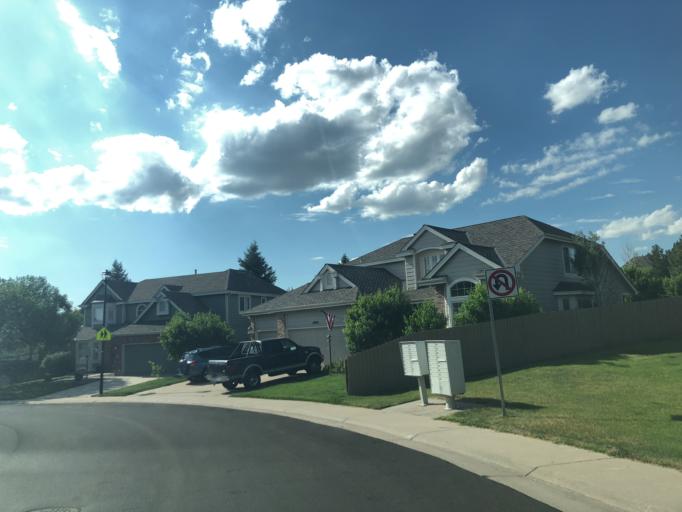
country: US
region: Colorado
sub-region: Arapahoe County
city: Dove Valley
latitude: 39.6101
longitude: -104.7659
